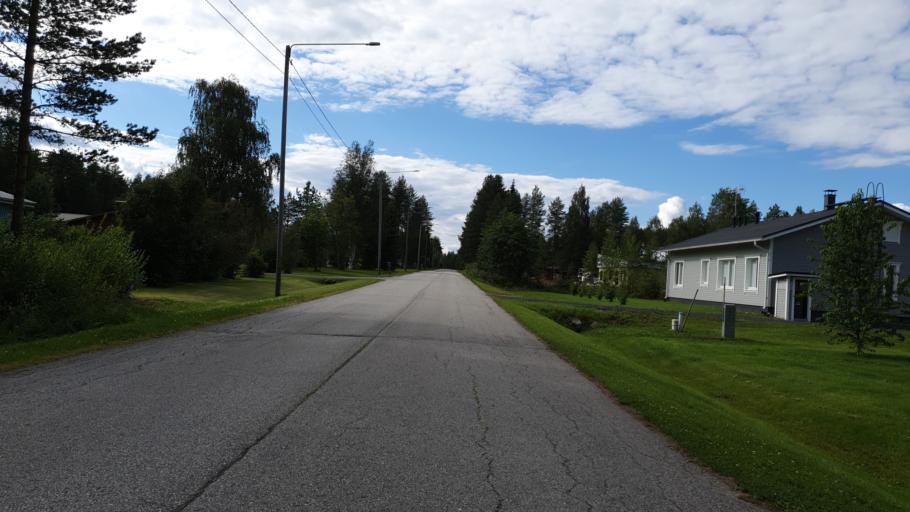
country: FI
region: Kainuu
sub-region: Kehys-Kainuu
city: Kuhmo
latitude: 64.1192
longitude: 29.5584
